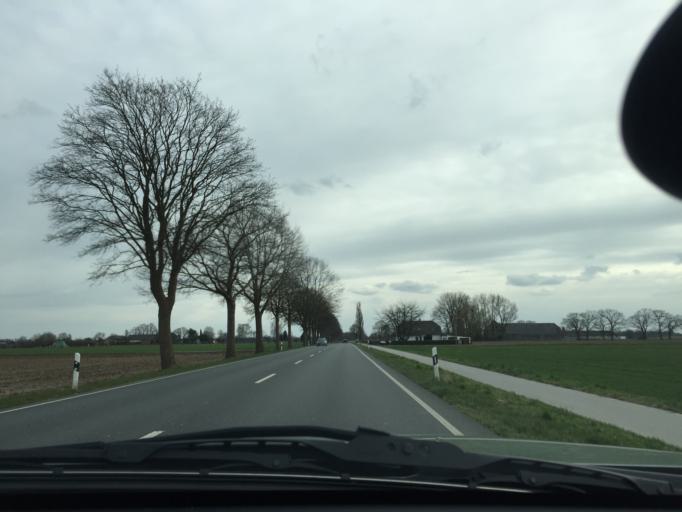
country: DE
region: North Rhine-Westphalia
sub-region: Regierungsbezirk Dusseldorf
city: Goch
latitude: 51.7278
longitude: 6.1591
